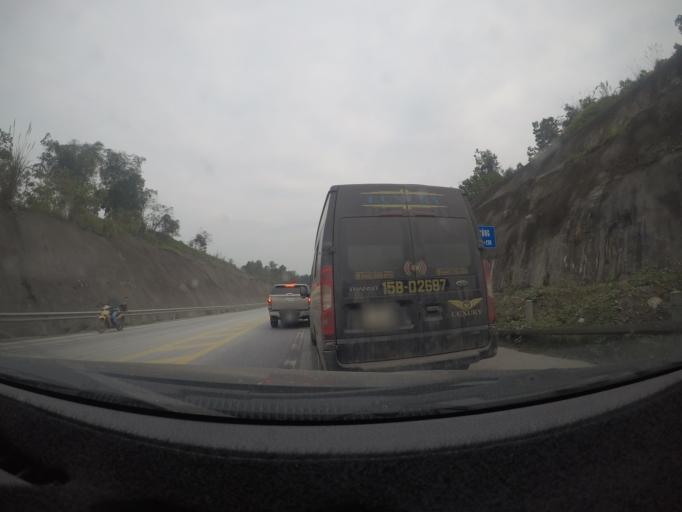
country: VN
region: Yen Bai
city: Co Phuc
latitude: 21.7915
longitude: 104.7653
